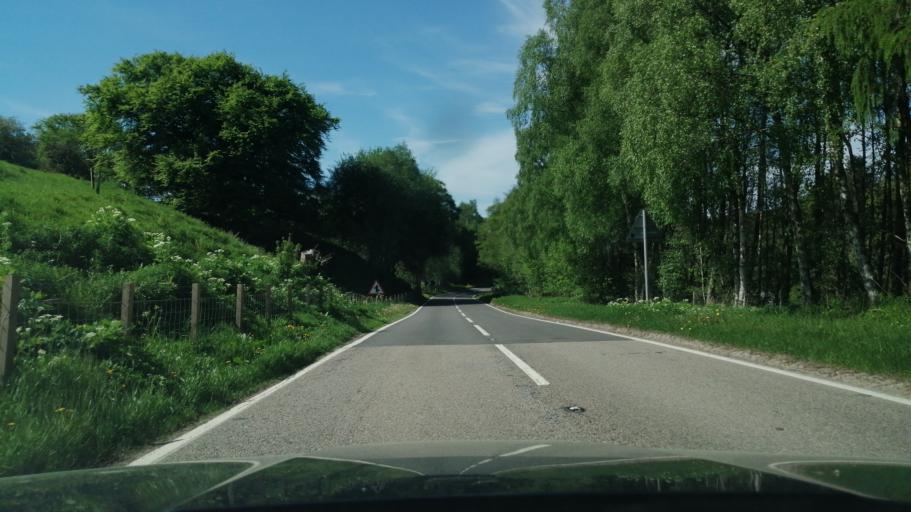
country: GB
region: Scotland
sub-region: Moray
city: Dufftown
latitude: 57.5031
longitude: -3.1304
